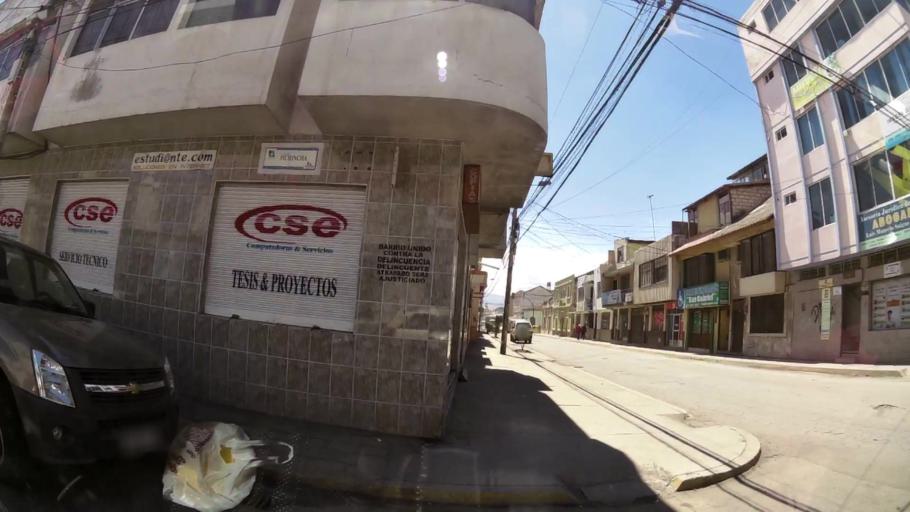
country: EC
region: Chimborazo
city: Riobamba
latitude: -1.6691
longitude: -78.6506
